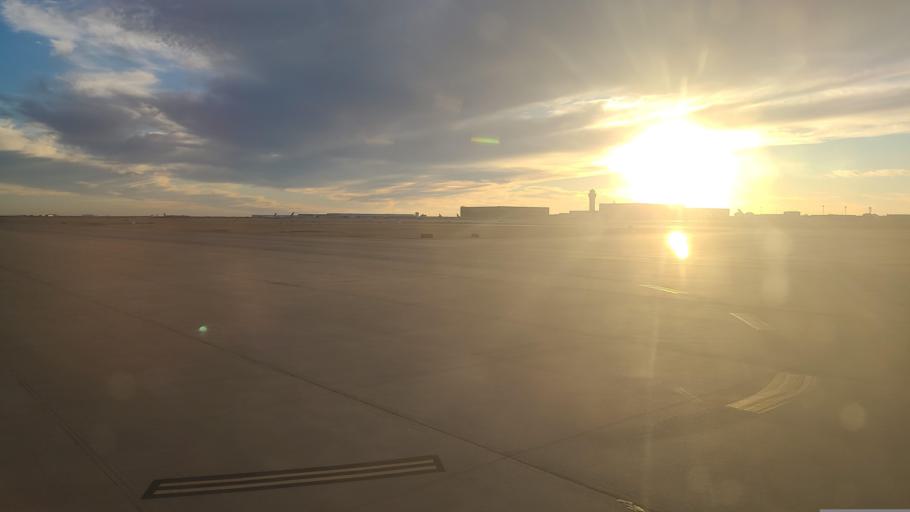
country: US
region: Texas
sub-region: Tarrant County
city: Grapevine
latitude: 32.9148
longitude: -97.0482
